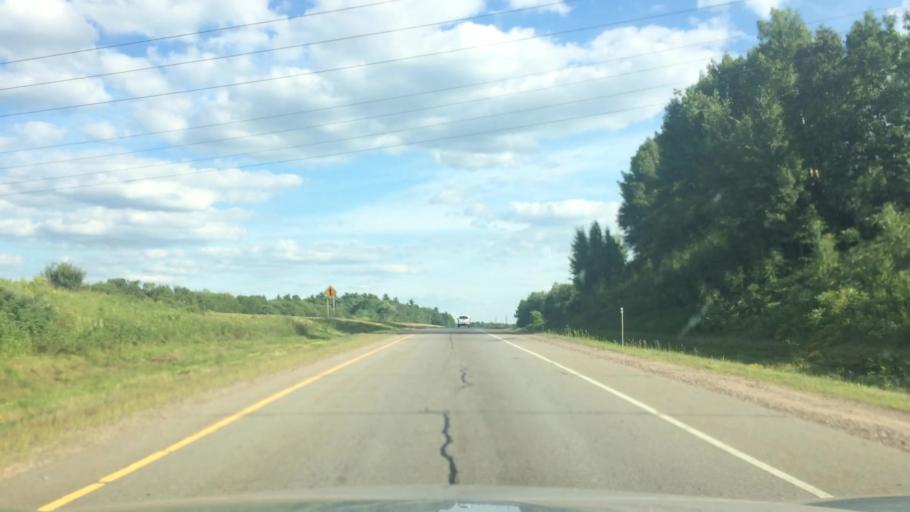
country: US
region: Wisconsin
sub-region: Lincoln County
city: Merrill
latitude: 45.1755
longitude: -89.6475
